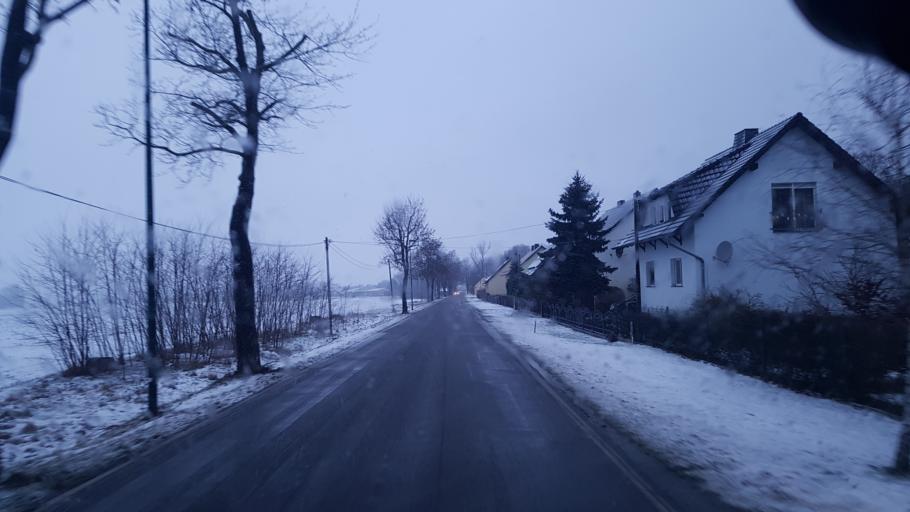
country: DE
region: Brandenburg
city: Tauer
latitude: 51.8977
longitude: 14.4747
